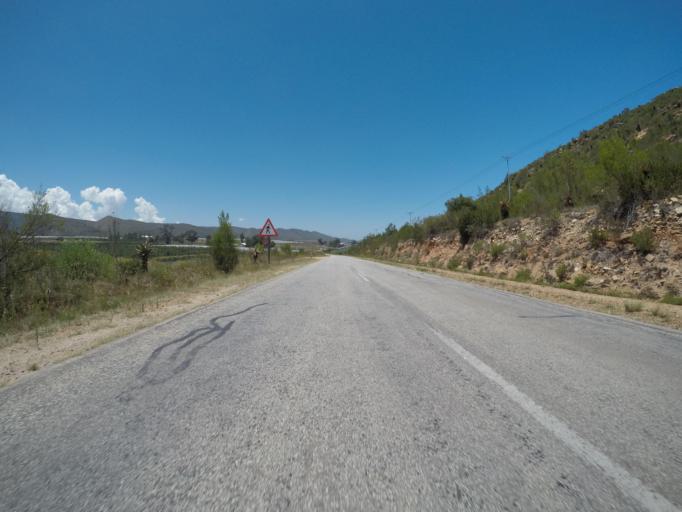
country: ZA
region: Western Cape
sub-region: Eden District Municipality
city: Plettenberg Bay
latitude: -33.8121
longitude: 23.7239
